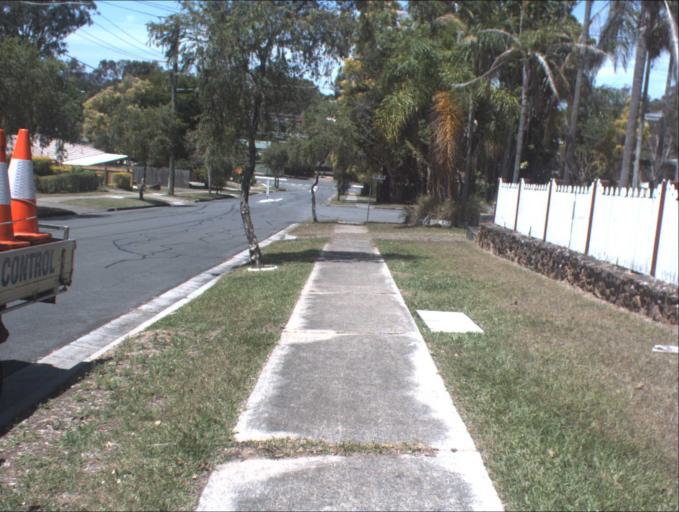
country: AU
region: Queensland
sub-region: Logan
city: Logan City
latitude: -27.6606
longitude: 153.1070
